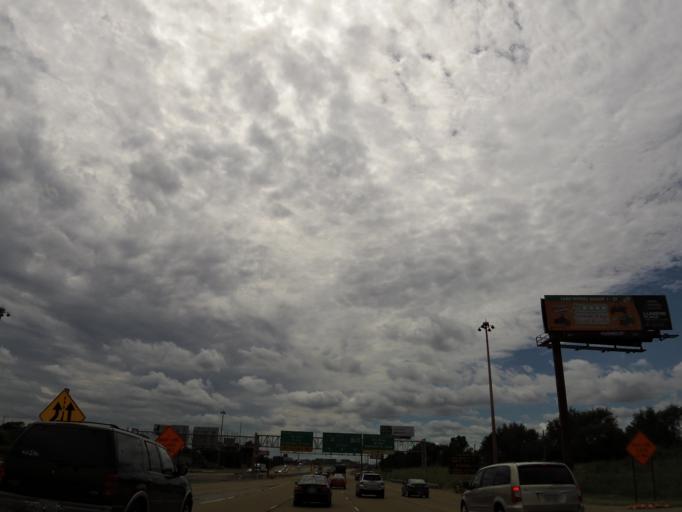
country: US
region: Illinois
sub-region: Saint Clair County
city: East Saint Louis
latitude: 38.6329
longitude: -90.1497
